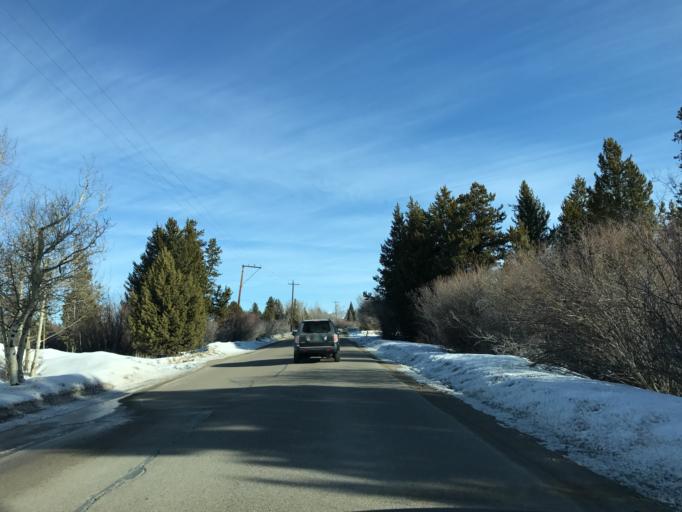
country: US
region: Wyoming
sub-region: Sublette County
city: Pinedale
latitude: 42.8590
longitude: -109.8612
